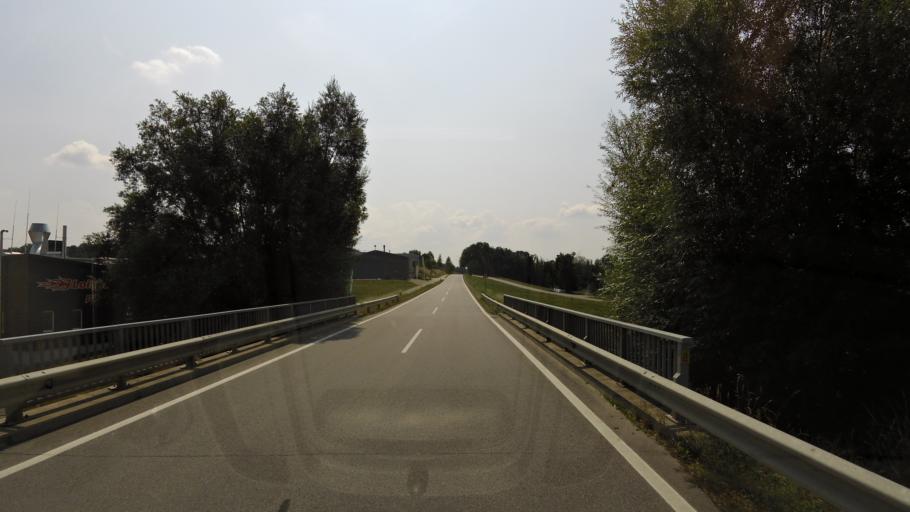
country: DE
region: Bavaria
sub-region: Lower Bavaria
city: Bad Fussing
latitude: 48.2616
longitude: 13.3345
